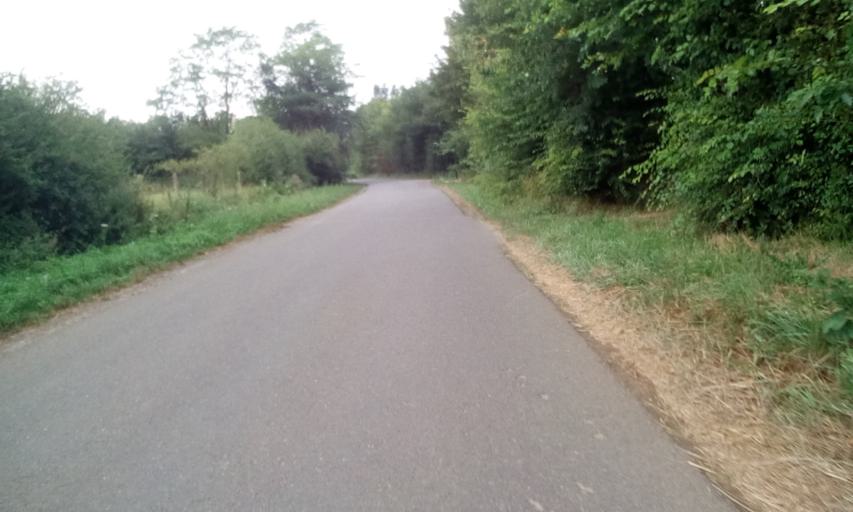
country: FR
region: Lower Normandy
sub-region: Departement du Calvados
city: Sannerville
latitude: 49.1943
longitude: -0.2223
